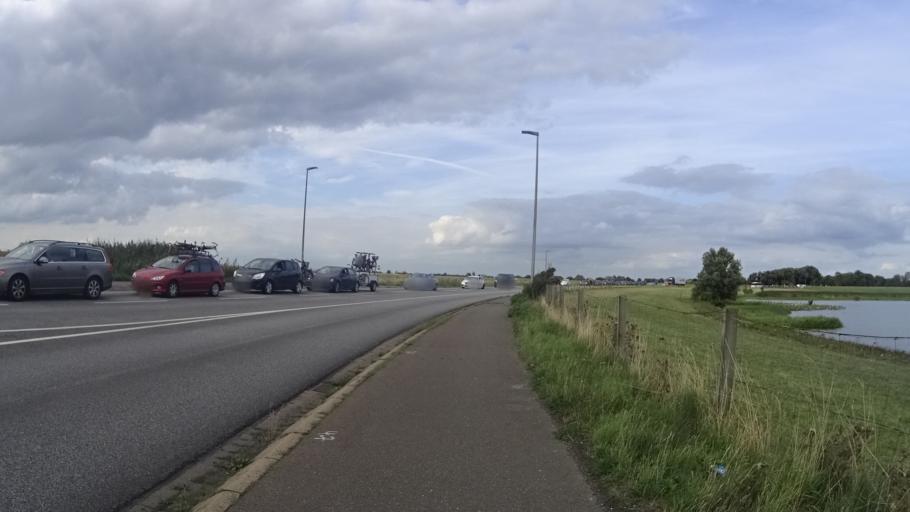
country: DE
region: Schleswig-Holstein
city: Blomesche Wildnis
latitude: 53.7962
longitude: 9.4035
